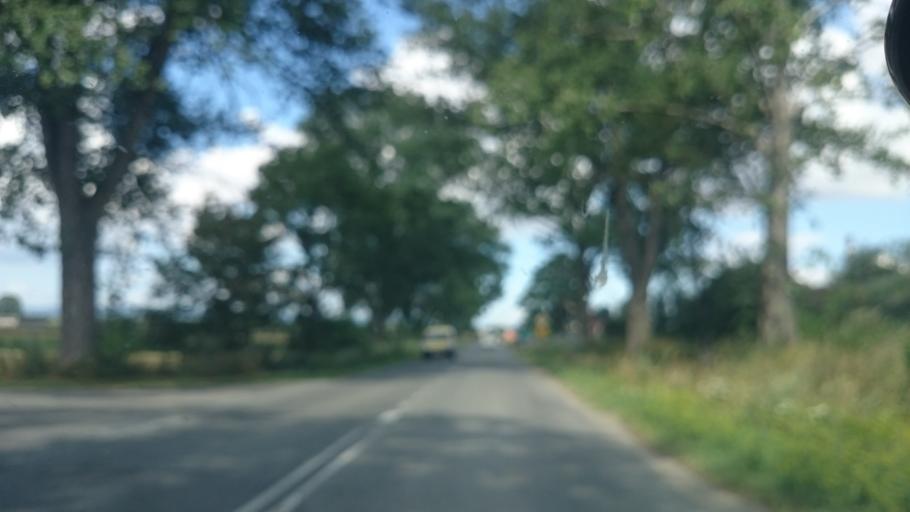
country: PL
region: Lower Silesian Voivodeship
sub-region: Powiat zabkowicki
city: Zabkowice Slaskie
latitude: 50.5781
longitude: 16.8334
